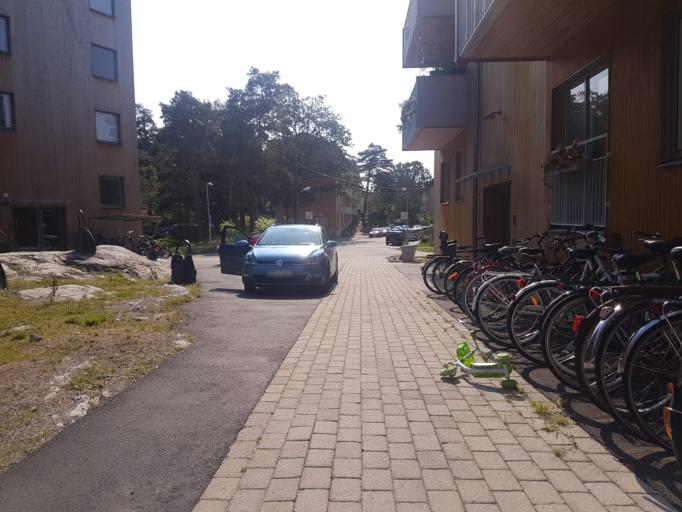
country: SE
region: Stockholm
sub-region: Stockholms Kommun
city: OEstermalm
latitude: 59.2978
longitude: 18.1136
